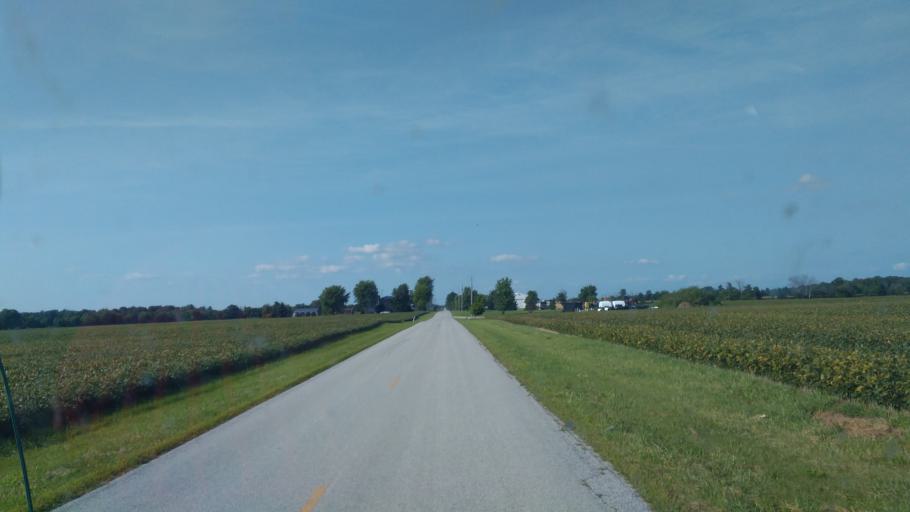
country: US
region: Ohio
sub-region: Hardin County
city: Forest
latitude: 40.7409
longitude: -83.5763
